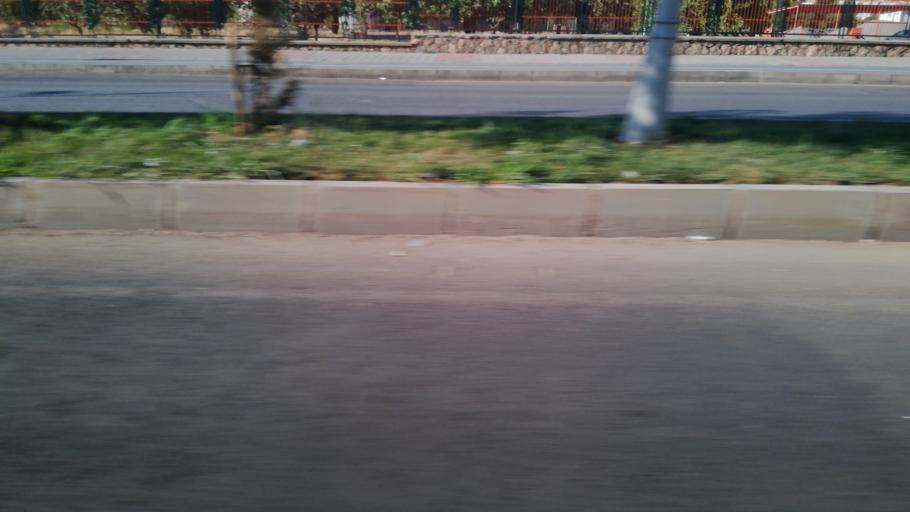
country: TR
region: Mardin
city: Midyat
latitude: 37.4161
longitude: 41.3680
